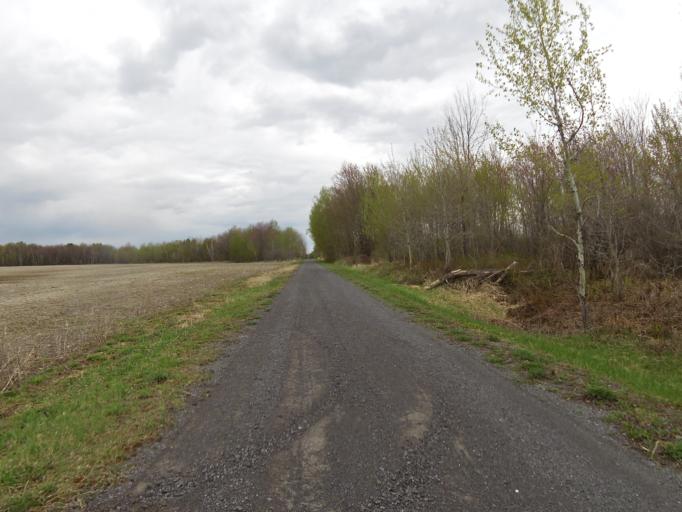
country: CA
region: Quebec
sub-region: Outaouais
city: Papineauville
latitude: 45.5182
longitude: -74.9544
